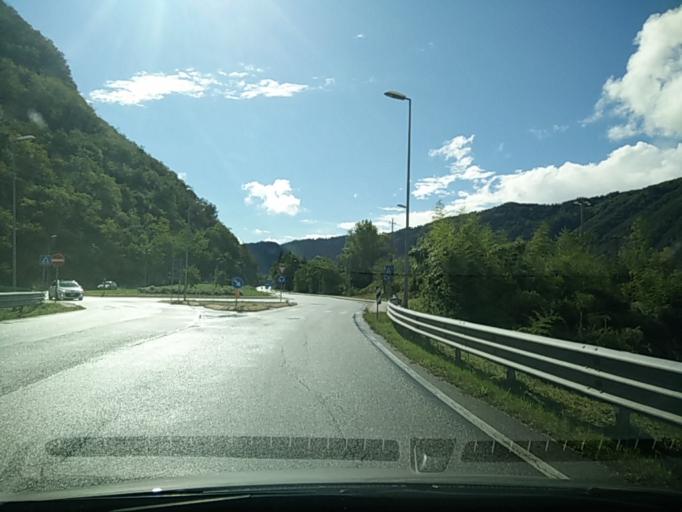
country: IT
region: Veneto
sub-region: Provincia di Treviso
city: Segusino
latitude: 45.9063
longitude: 11.9517
